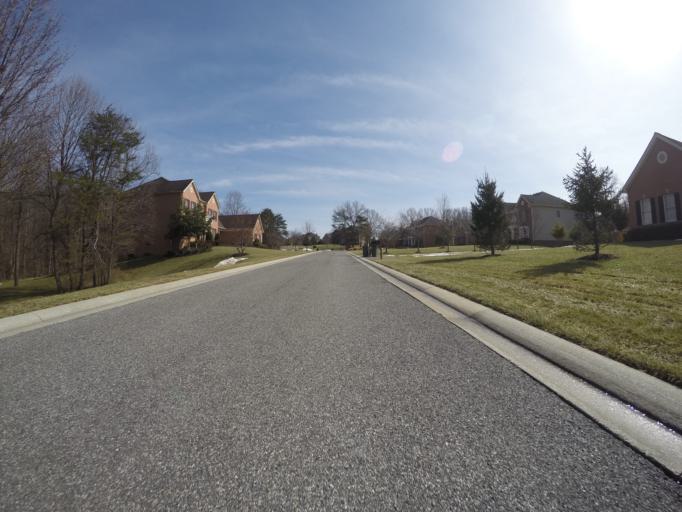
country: US
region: Maryland
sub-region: Baltimore County
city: Hunt Valley
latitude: 39.5100
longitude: -76.6533
